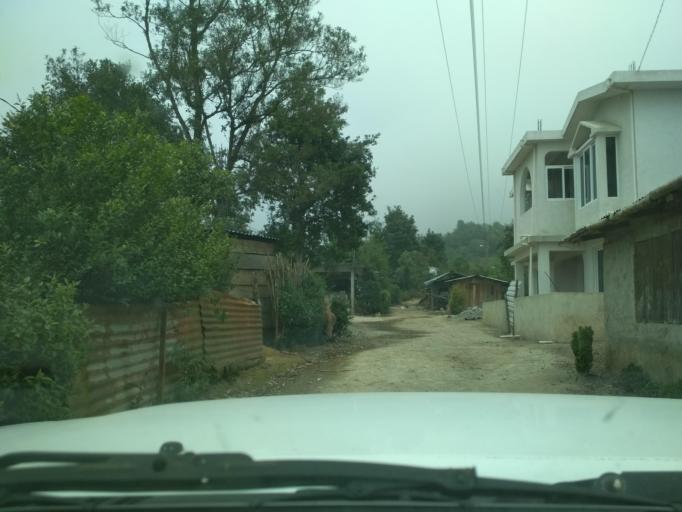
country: MX
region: Veracruz
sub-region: La Perla
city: Chilapa
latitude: 18.9667
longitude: -97.1703
